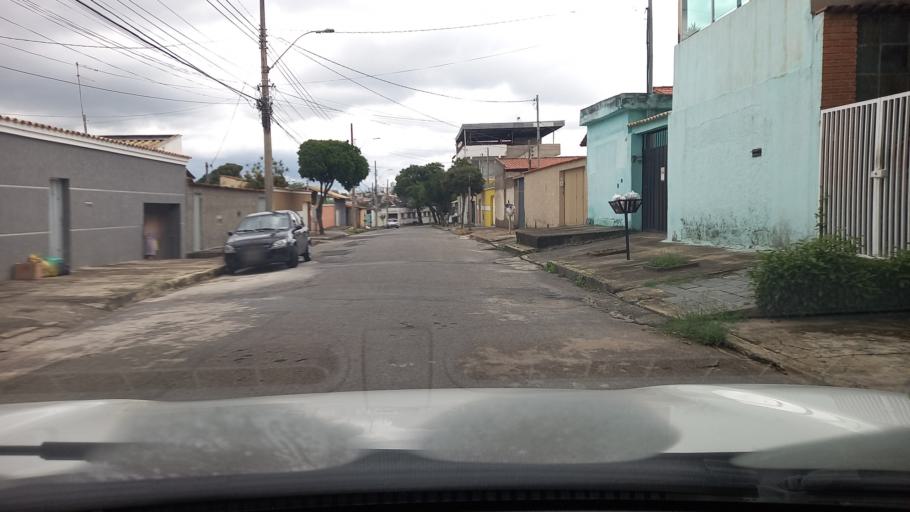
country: BR
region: Minas Gerais
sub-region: Contagem
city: Contagem
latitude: -19.8981
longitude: -44.0131
